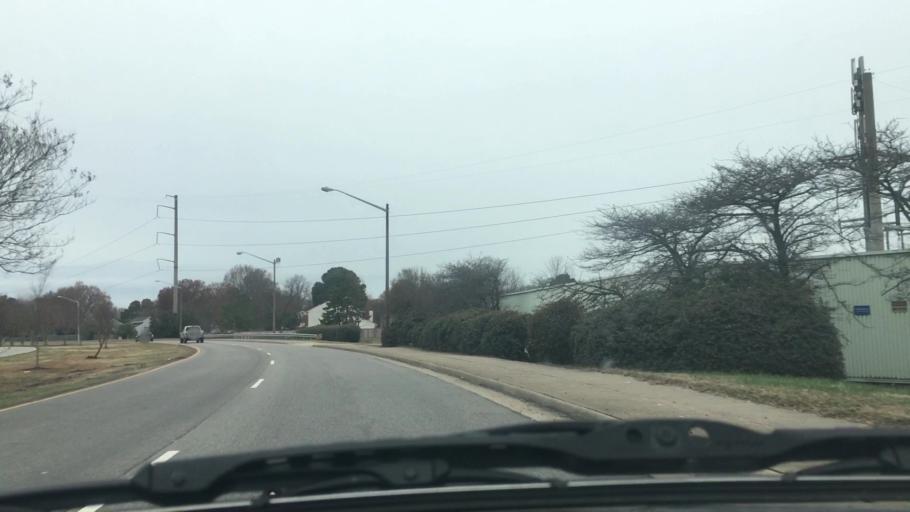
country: US
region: Virginia
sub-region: City of Virginia Beach
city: Virginia Beach
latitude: 36.7977
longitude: -76.1078
